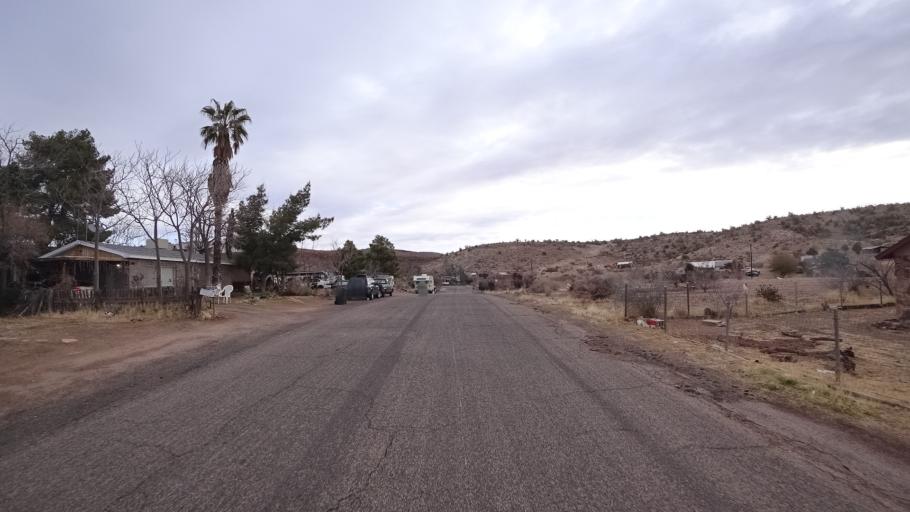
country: US
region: Arizona
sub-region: Mohave County
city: Kingman
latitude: 35.1969
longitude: -114.0739
